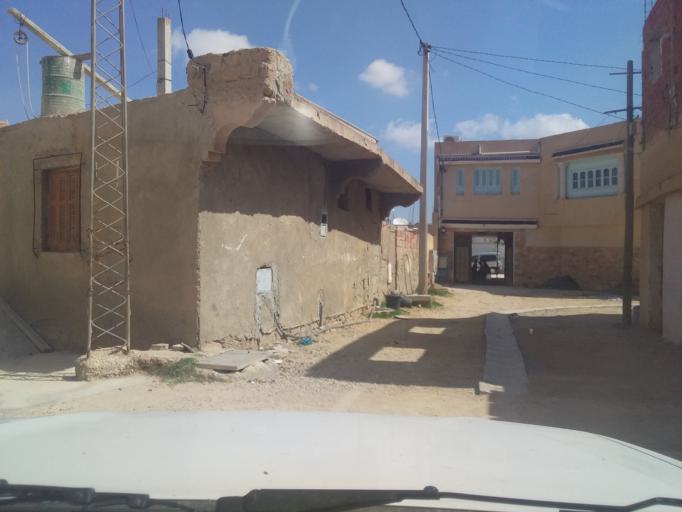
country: TN
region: Qabis
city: Gabes
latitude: 33.6219
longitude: 10.2868
